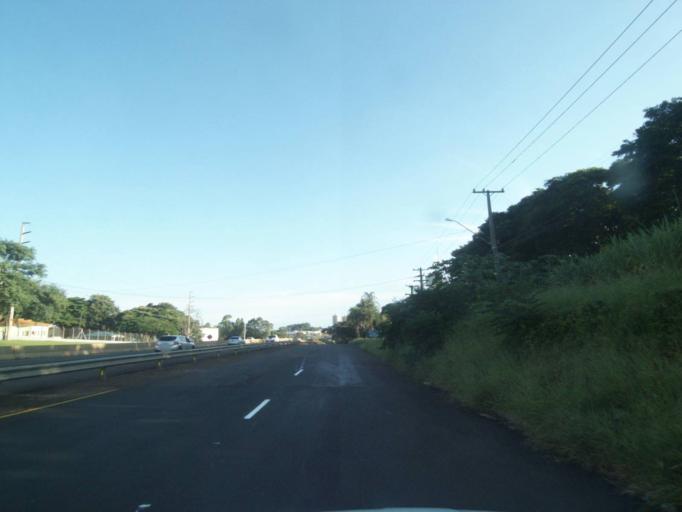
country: BR
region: Parana
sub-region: Londrina
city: Londrina
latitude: -23.3352
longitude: -51.1847
